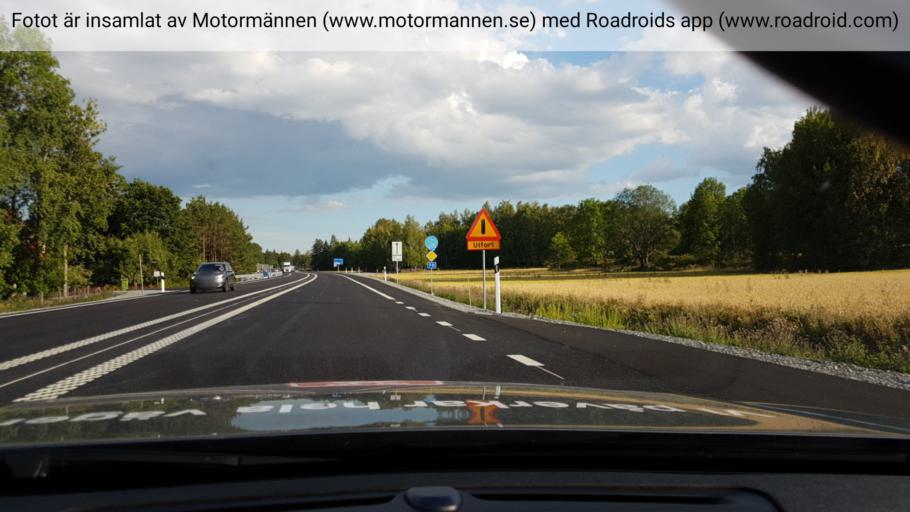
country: SE
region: Uppsala
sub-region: Enkopings Kommun
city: Irsta
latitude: 59.7377
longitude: 16.9538
